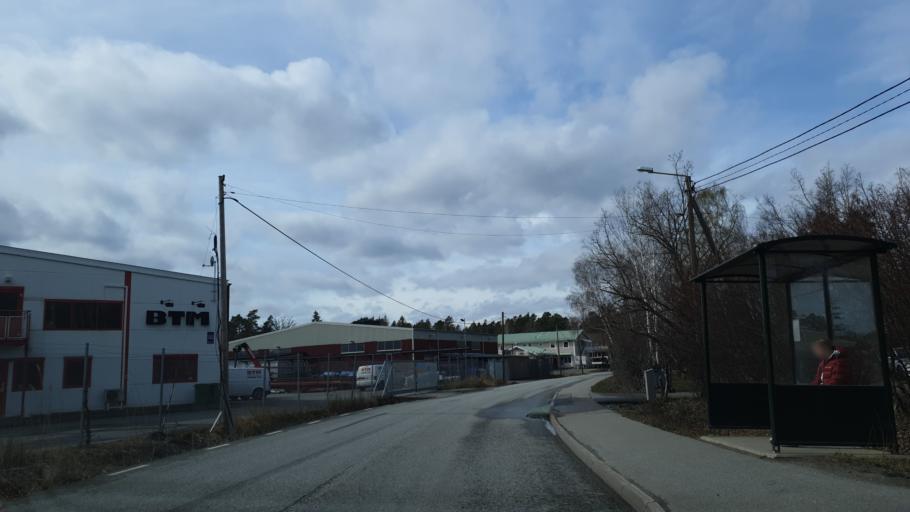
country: SE
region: Stockholm
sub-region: Nacka Kommun
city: Boo
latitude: 59.3231
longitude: 18.2939
